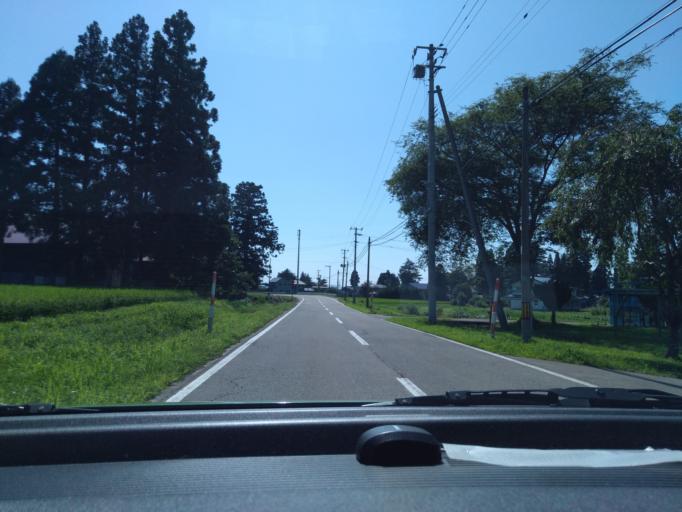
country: JP
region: Akita
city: Kakunodatemachi
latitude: 39.4802
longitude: 140.6146
